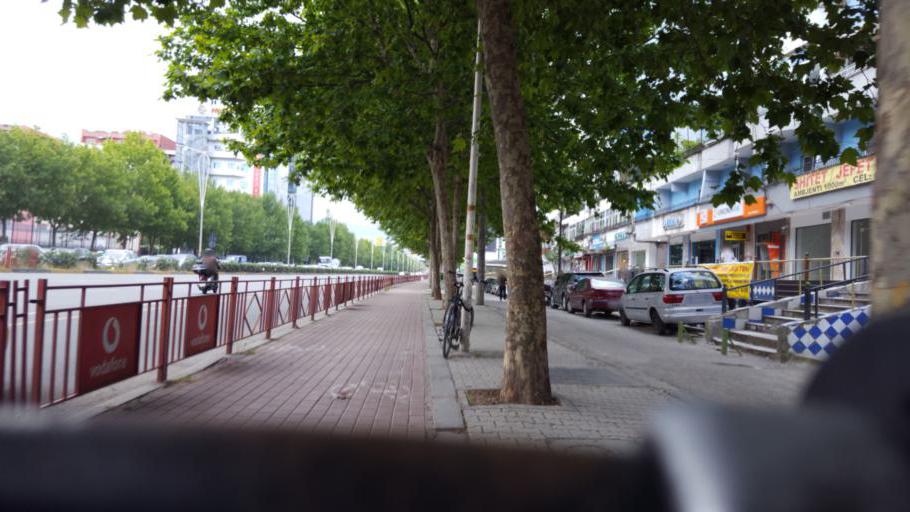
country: AL
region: Tirane
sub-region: Rrethi i Tiranes
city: Paskuqan
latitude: 41.3370
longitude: 19.7927
